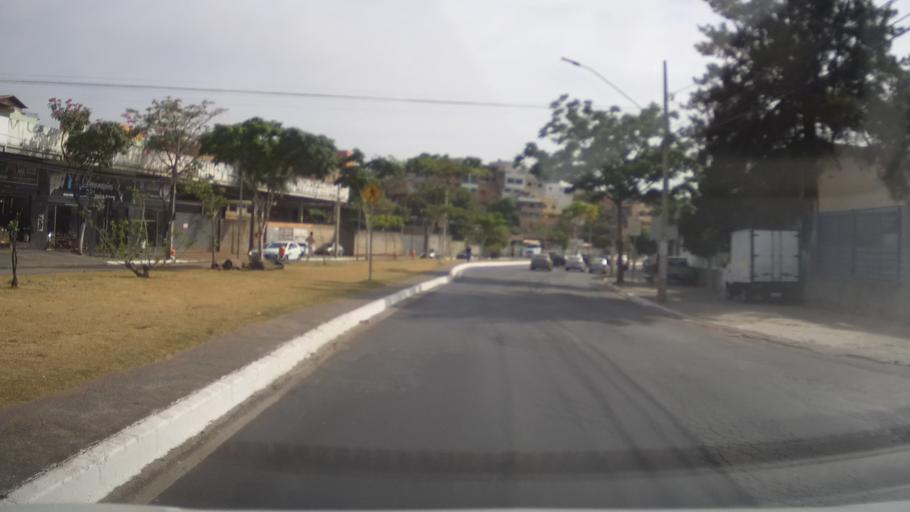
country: BR
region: Minas Gerais
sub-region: Contagem
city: Contagem
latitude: -19.9469
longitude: -44.0514
